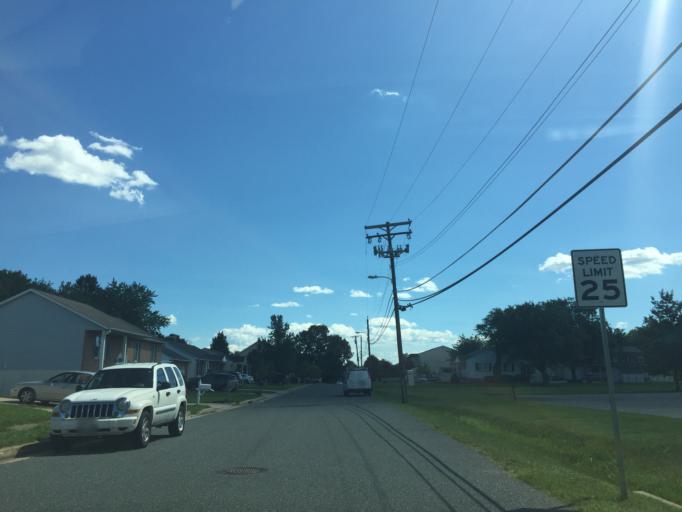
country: US
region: Maryland
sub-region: Baltimore County
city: Perry Hall
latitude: 39.4091
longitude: -76.4662
